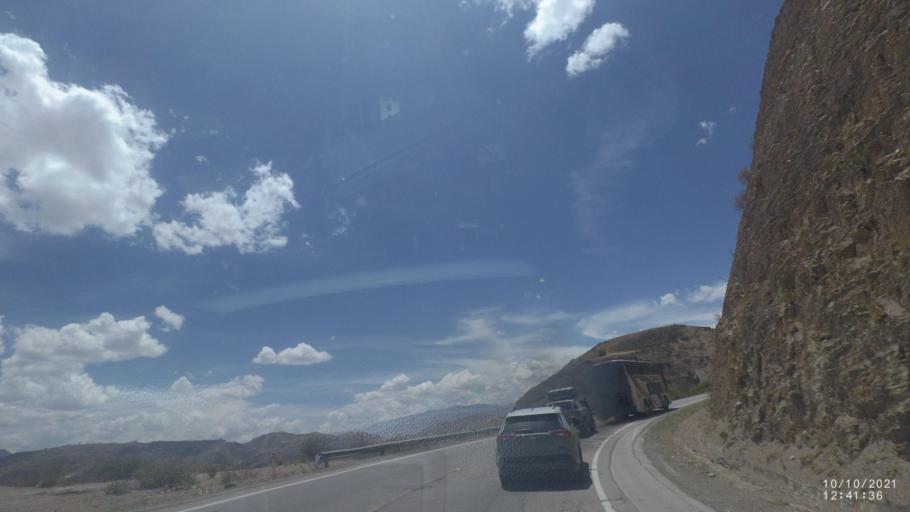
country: BO
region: Cochabamba
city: Irpa Irpa
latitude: -17.6347
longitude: -66.3907
